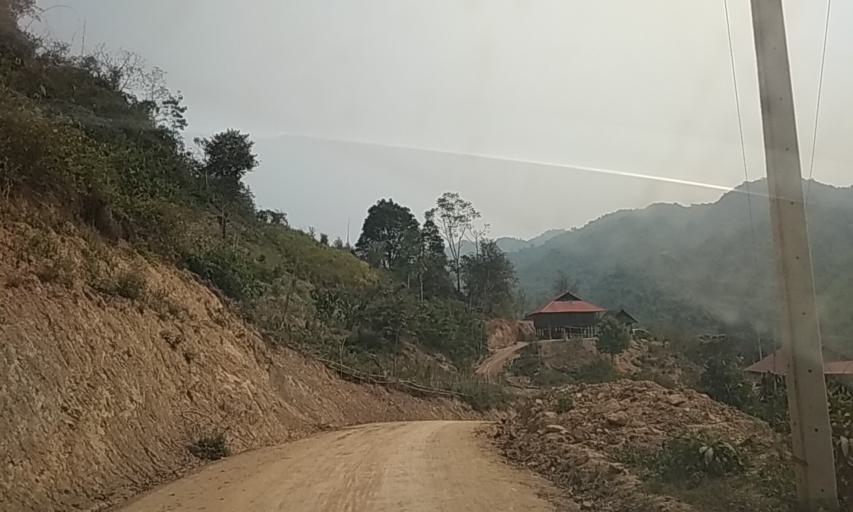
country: VN
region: Huyen Dien Bien
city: Dien Bien Phu
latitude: 21.4318
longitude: 102.7646
